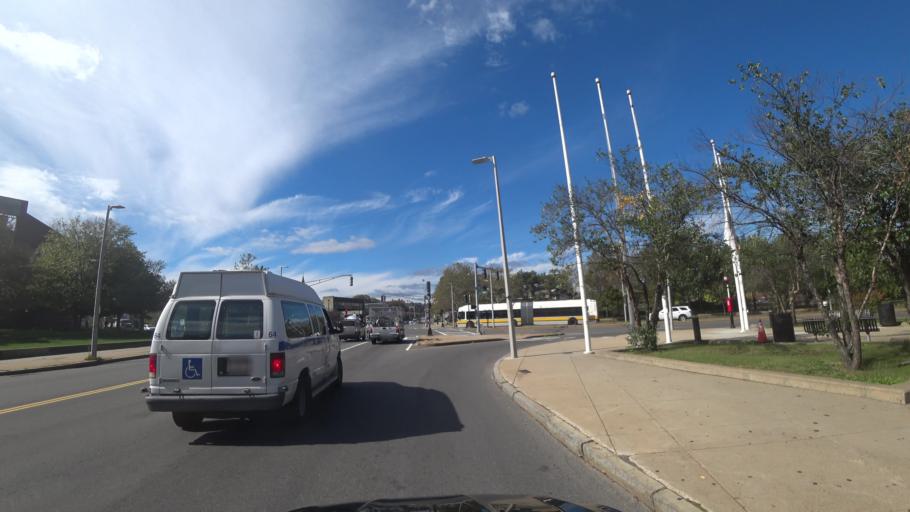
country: US
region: Massachusetts
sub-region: Norfolk County
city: Brookline
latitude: 42.3314
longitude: -71.0934
